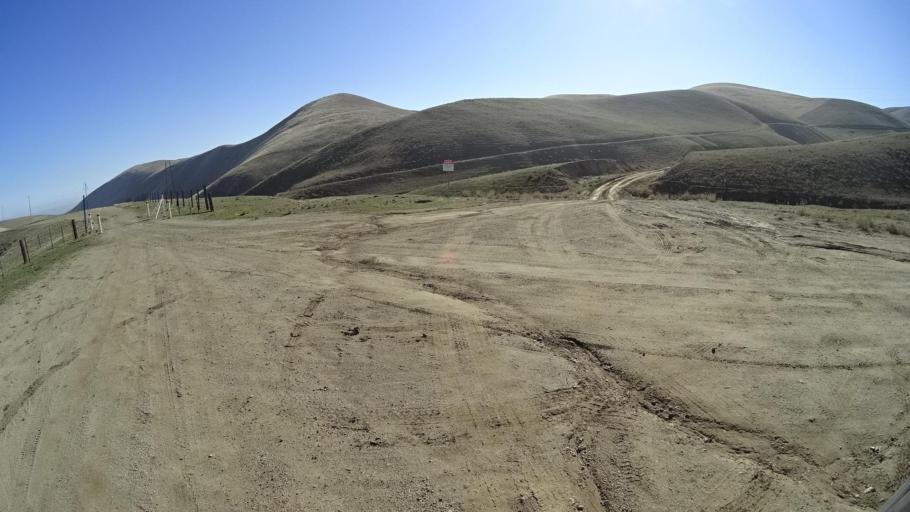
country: US
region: California
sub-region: Kern County
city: Taft Heights
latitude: 35.2285
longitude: -119.6741
